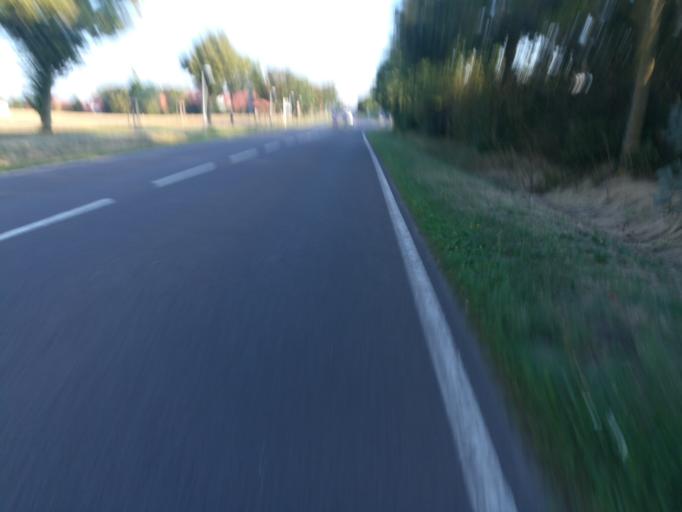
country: DE
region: Saxony-Anhalt
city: Irxleben
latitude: 52.1582
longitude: 11.4865
